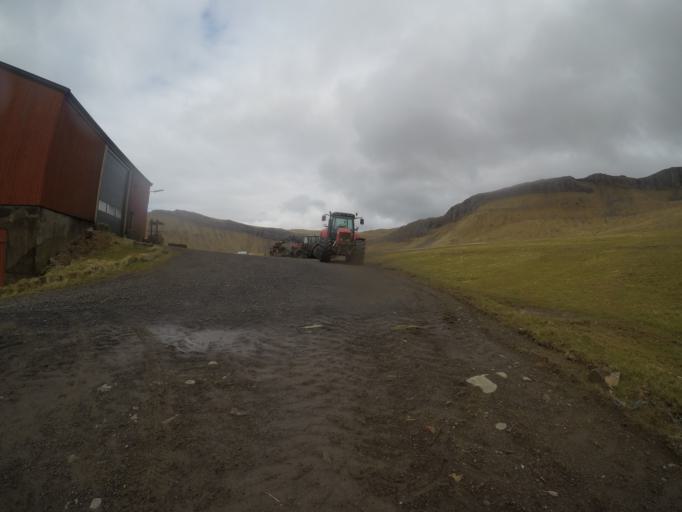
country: FO
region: Streymoy
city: Kollafjordhur
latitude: 62.0417
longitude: -6.9515
